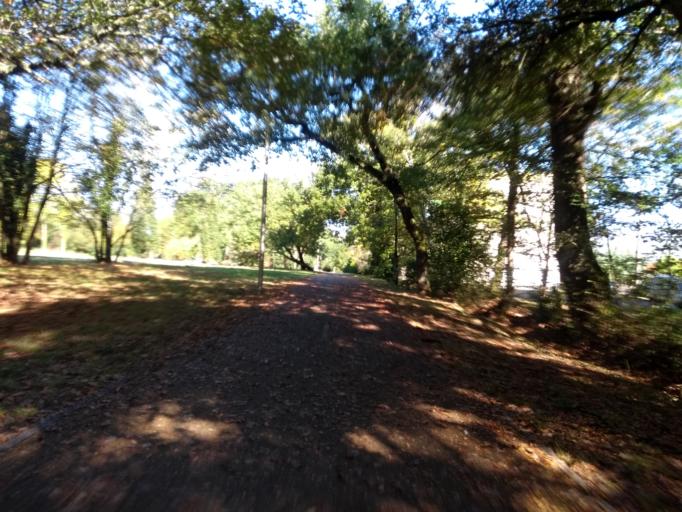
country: FR
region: Aquitaine
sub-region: Departement de la Gironde
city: Pessac
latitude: 44.7955
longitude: -0.6349
